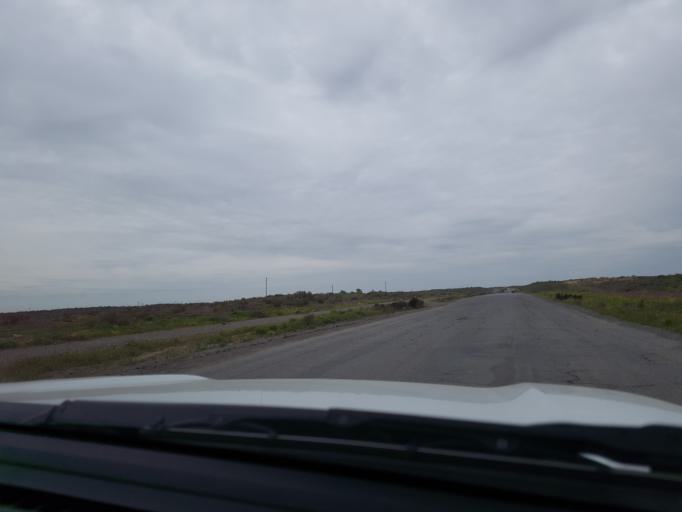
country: TM
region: Mary
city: Bayramaly
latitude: 37.9027
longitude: 62.6187
